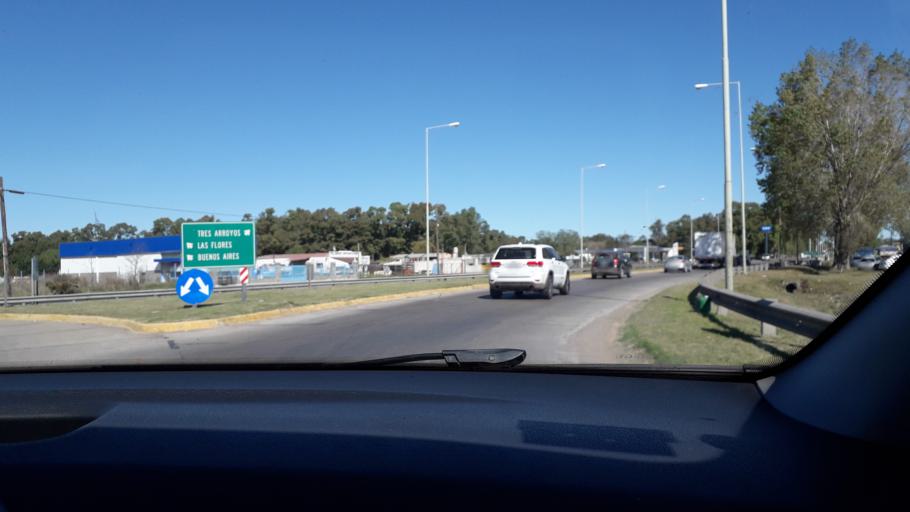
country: AR
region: Buenos Aires
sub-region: Partido de Azul
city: Azul
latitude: -36.7920
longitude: -59.8407
